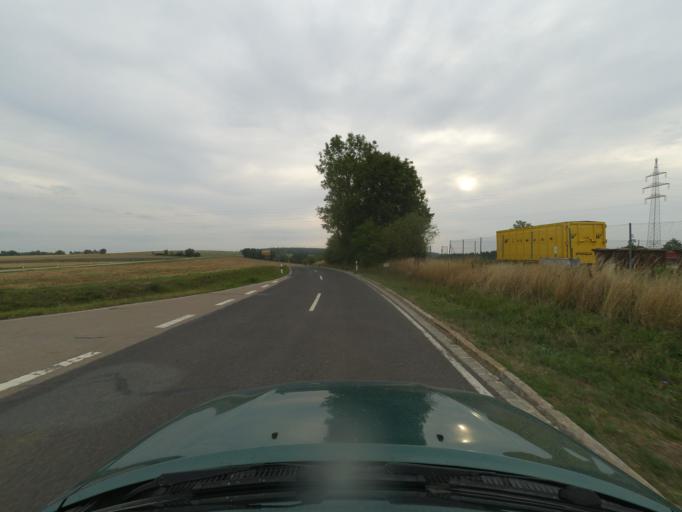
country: DE
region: Bavaria
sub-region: Upper Palatinate
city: Edelsfeld
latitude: 49.5784
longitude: 11.7008
